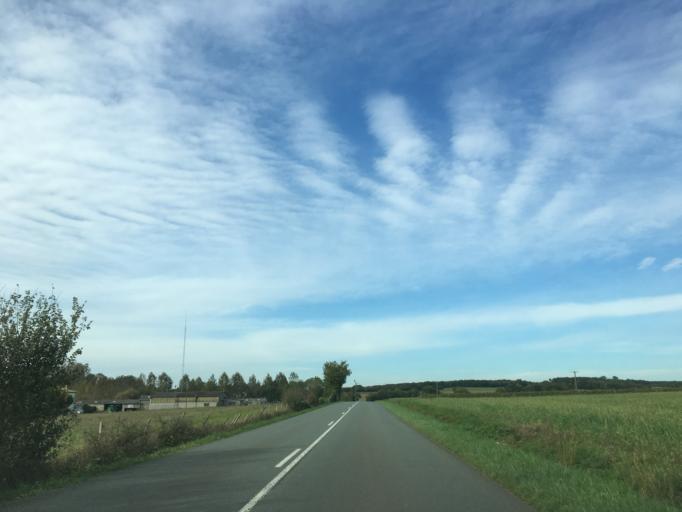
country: FR
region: Poitou-Charentes
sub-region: Departement de la Charente-Maritime
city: Aulnay
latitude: 46.0694
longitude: -0.4283
